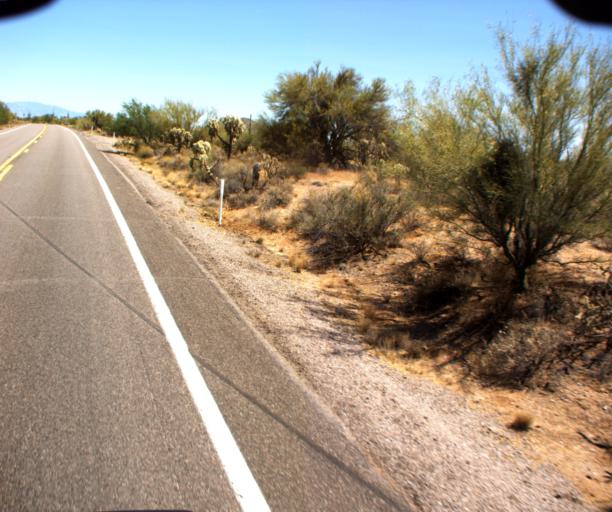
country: US
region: Arizona
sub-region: Pima County
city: Marana
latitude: 32.7701
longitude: -111.1580
